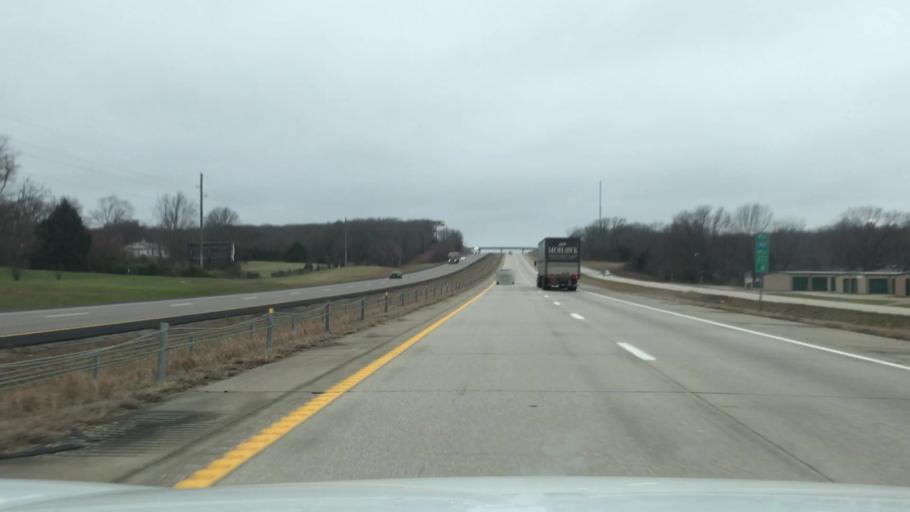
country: US
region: Missouri
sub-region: Franklin County
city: Sullivan
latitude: 38.1890
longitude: -91.1931
